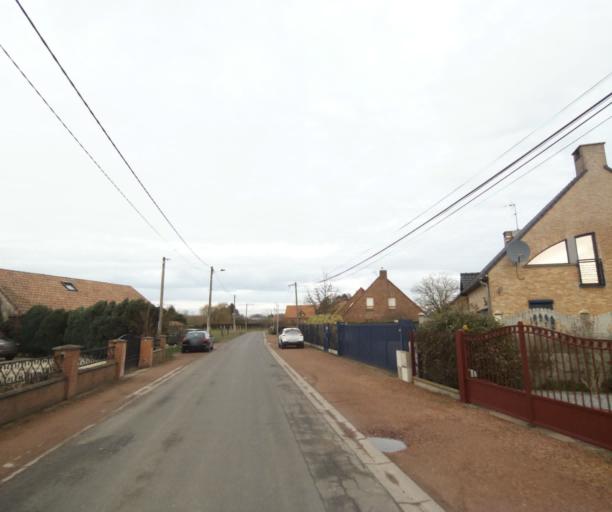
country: FR
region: Nord-Pas-de-Calais
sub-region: Departement du Nord
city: Hergnies
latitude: 50.4792
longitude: 3.5113
